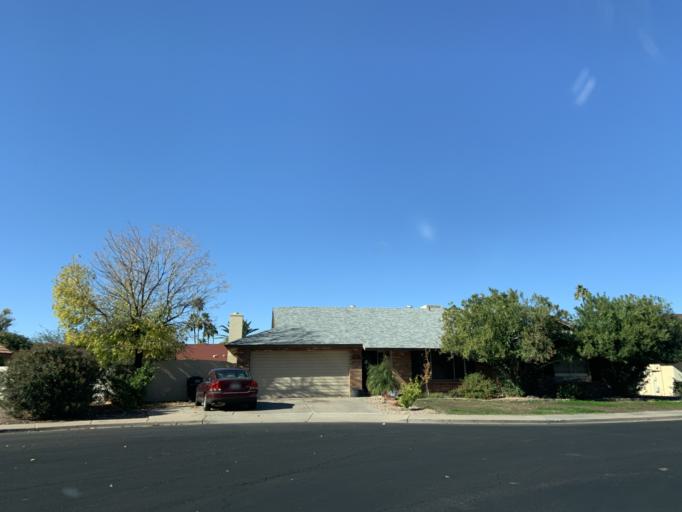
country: US
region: Arizona
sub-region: Maricopa County
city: San Carlos
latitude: 33.3701
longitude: -111.8646
